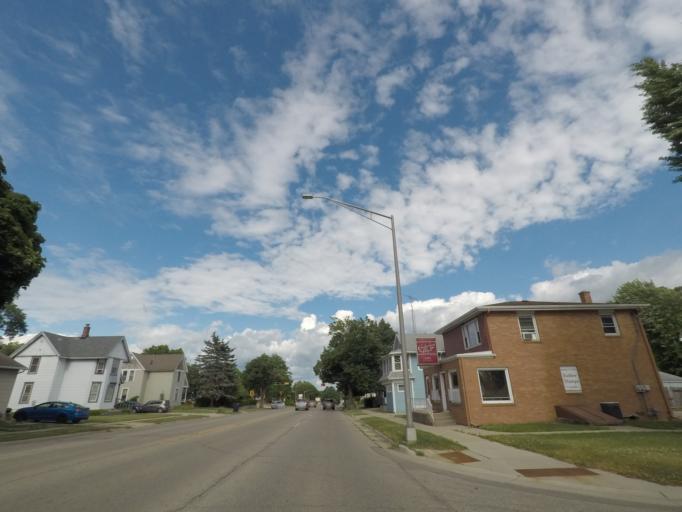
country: US
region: Wisconsin
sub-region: Rock County
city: Janesville
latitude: 42.6794
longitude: -89.0370
